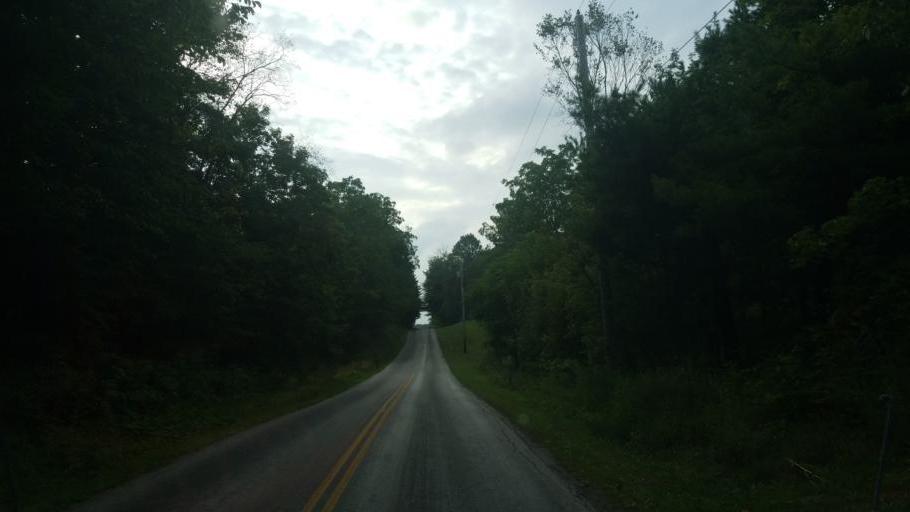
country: US
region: Ohio
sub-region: Wayne County
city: West Salem
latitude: 40.9818
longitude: -82.0839
